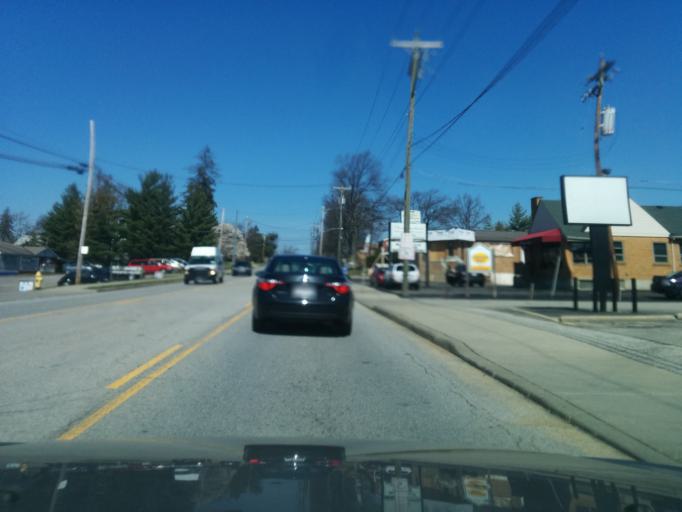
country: US
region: Ohio
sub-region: Hamilton County
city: White Oak
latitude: 39.2064
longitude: -84.5995
